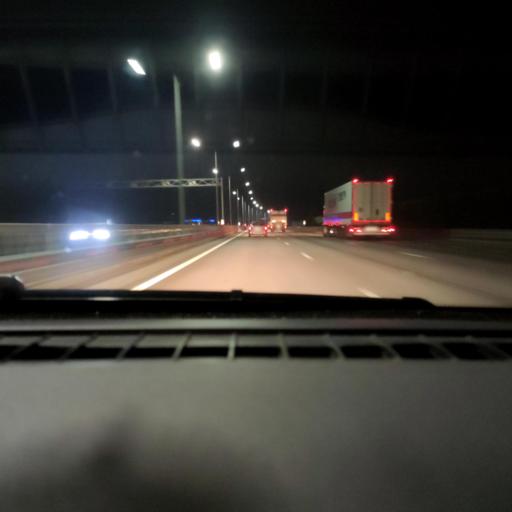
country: RU
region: Voronezj
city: Podgornoye
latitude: 51.8102
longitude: 39.2528
